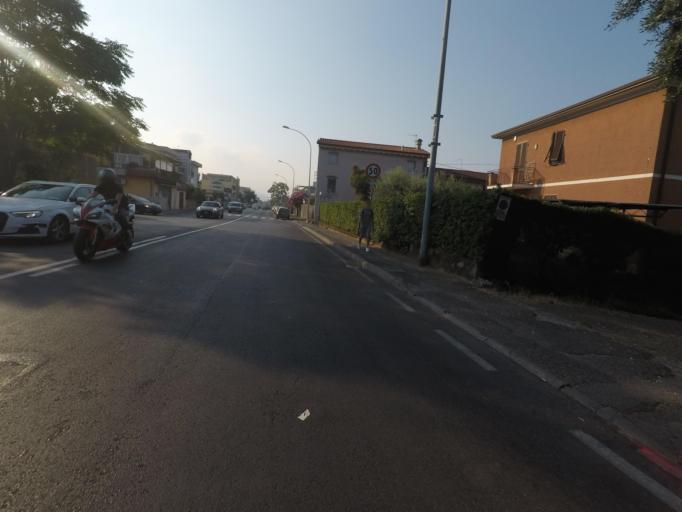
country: IT
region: Tuscany
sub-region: Provincia di Massa-Carrara
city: Massa
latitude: 44.0273
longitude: 10.1325
